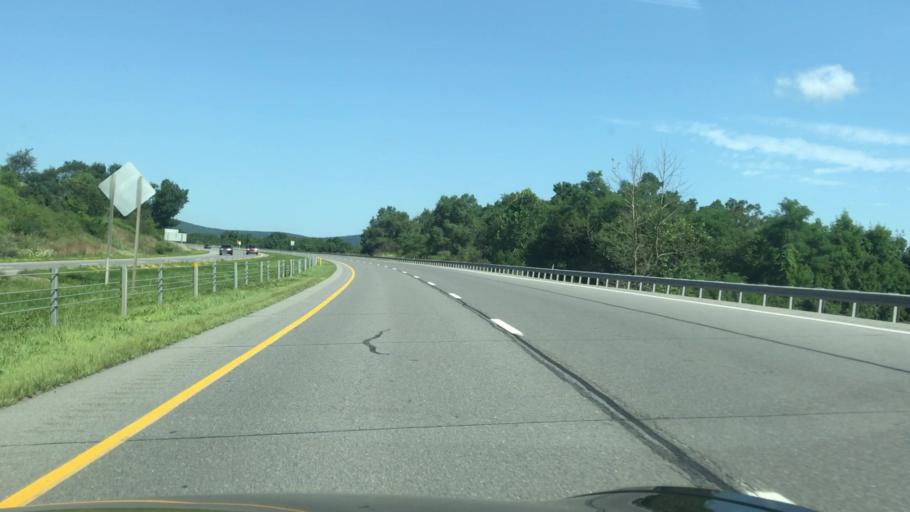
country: US
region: Pennsylvania
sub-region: Lycoming County
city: Garden View
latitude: 41.3002
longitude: -77.0674
